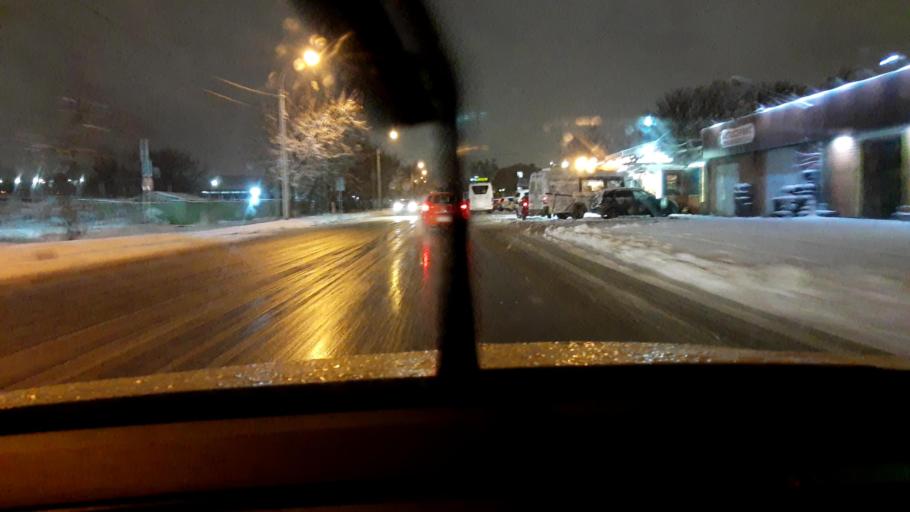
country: RU
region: Moscow
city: Nekrasovka
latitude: 55.6821
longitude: 37.9112
